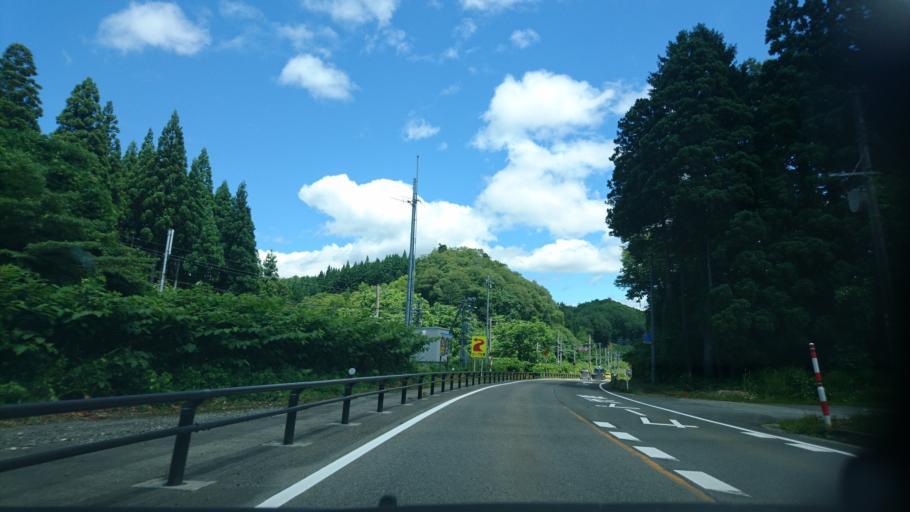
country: JP
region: Akita
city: Kakunodatemachi
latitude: 39.6798
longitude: 140.7033
